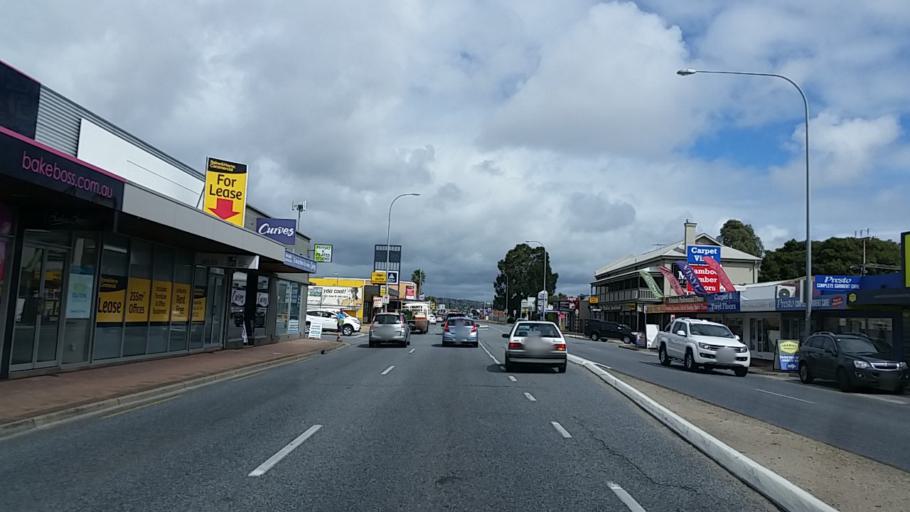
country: AU
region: South Australia
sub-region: Mitcham
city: Clarence Gardens
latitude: -34.9746
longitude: 138.5735
